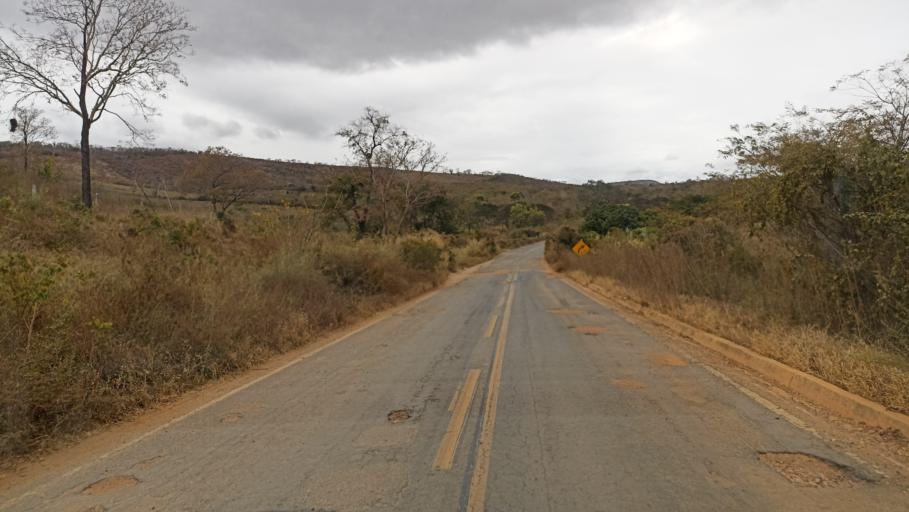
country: BR
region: Minas Gerais
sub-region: Itinga
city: Itinga
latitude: -16.6467
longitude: -41.8291
